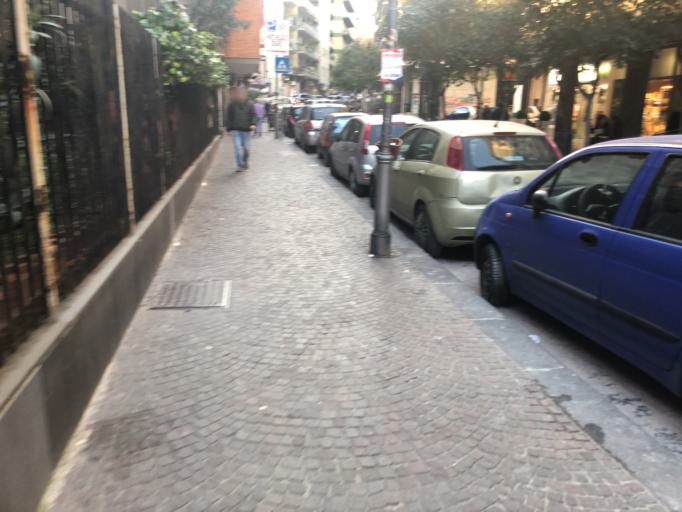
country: IT
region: Campania
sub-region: Provincia di Napoli
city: Napoli
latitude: 40.8610
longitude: 14.2217
